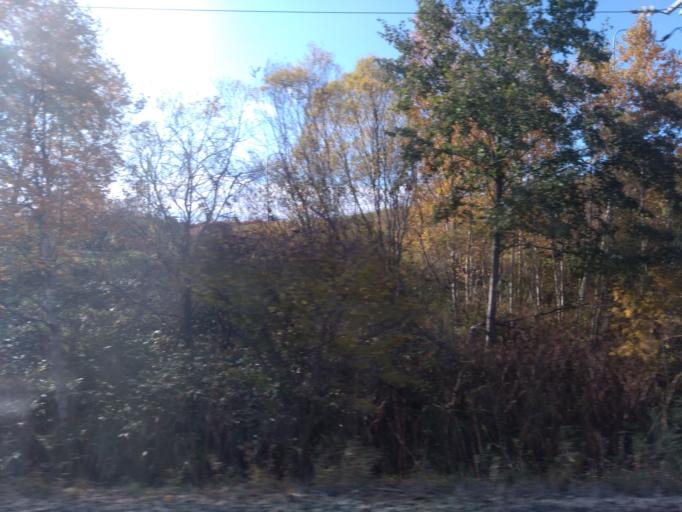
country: JP
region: Hokkaido
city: Kitahiroshima
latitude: 42.9486
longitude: 141.5713
